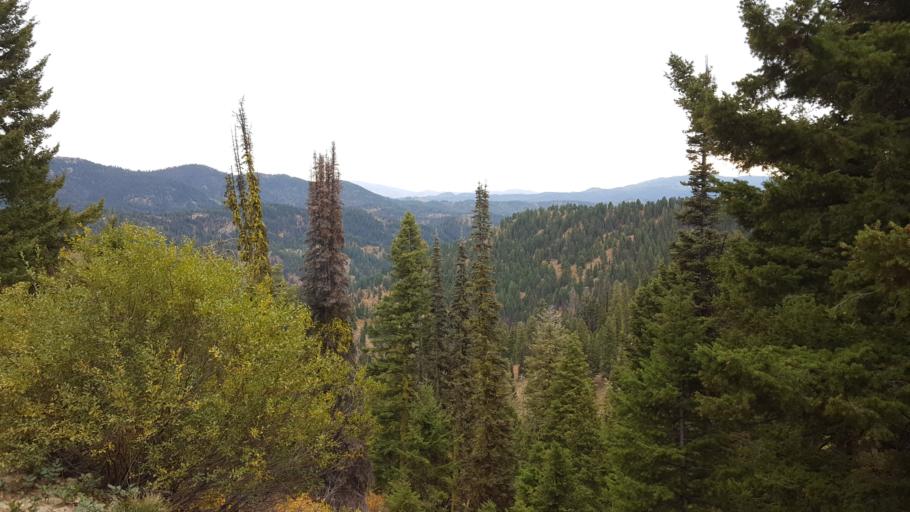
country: US
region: Idaho
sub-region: Boise County
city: Idaho City
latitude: 43.9467
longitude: -115.6861
